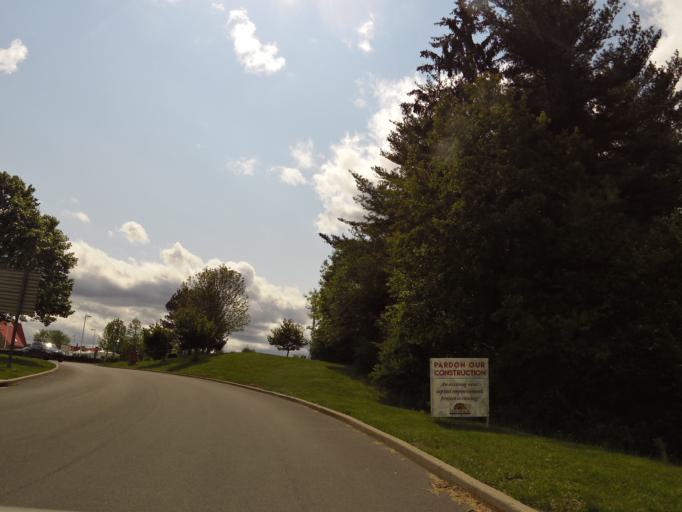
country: US
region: West Virginia
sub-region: Raleigh County
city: Mabscott
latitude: 37.8028
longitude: -81.2163
